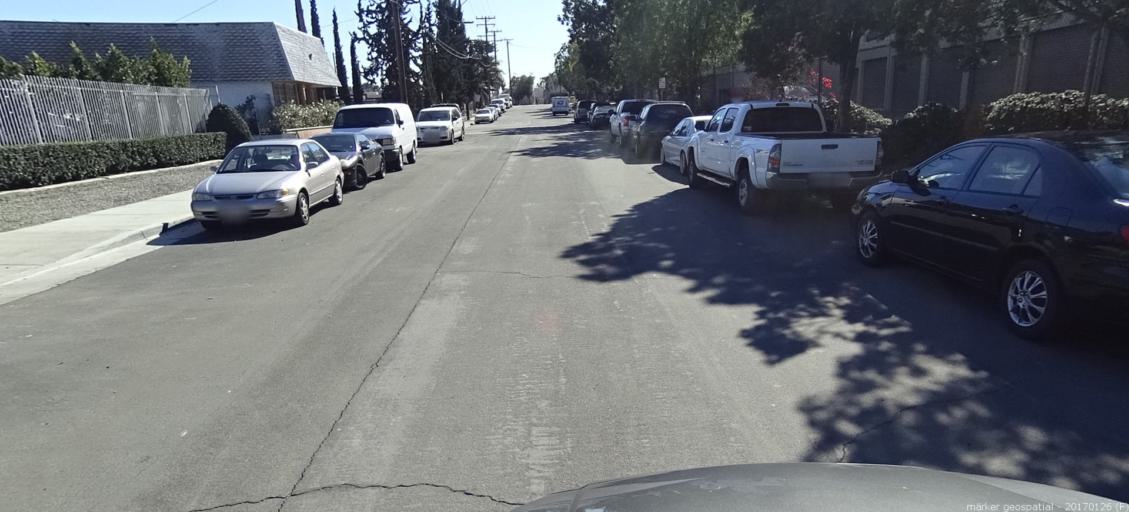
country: US
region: California
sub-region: Orange County
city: Lake Forest
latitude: 33.6262
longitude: -117.6926
